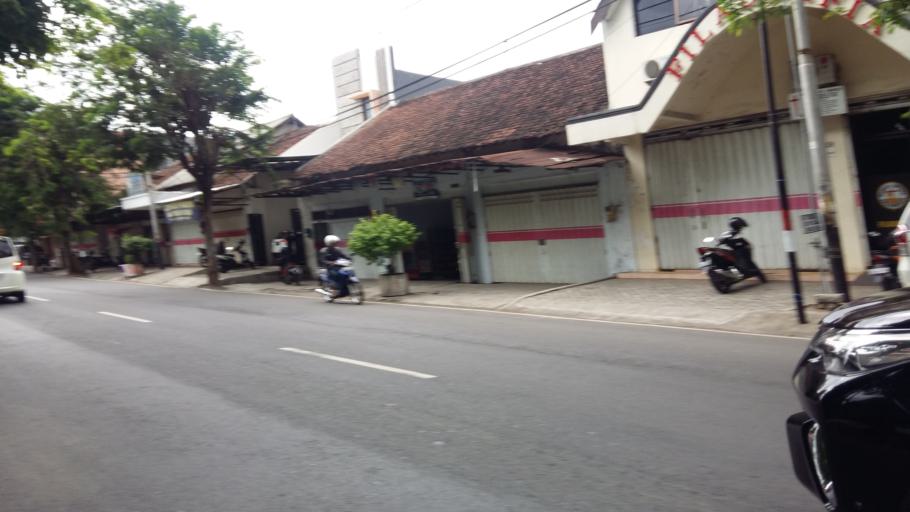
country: ID
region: East Java
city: Krajan
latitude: -8.3121
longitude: 114.2905
